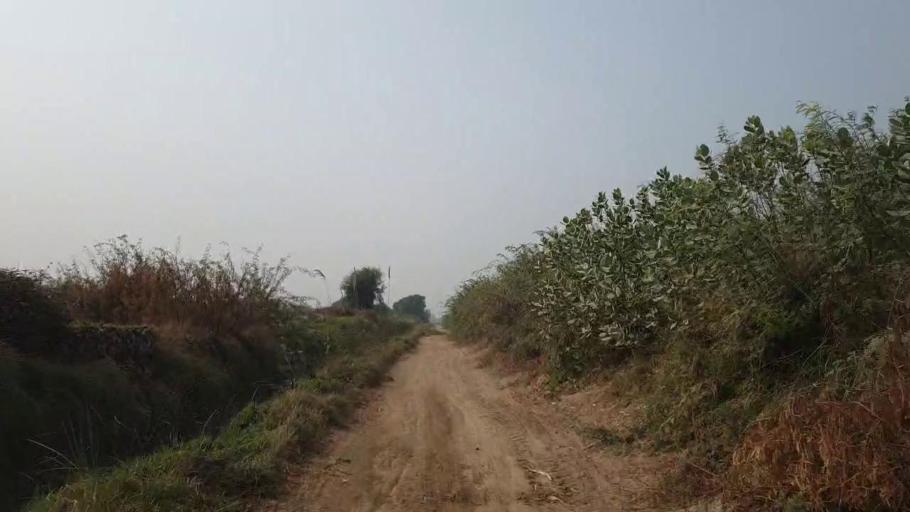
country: PK
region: Sindh
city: Tando Muhammad Khan
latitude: 25.1907
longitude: 68.5858
